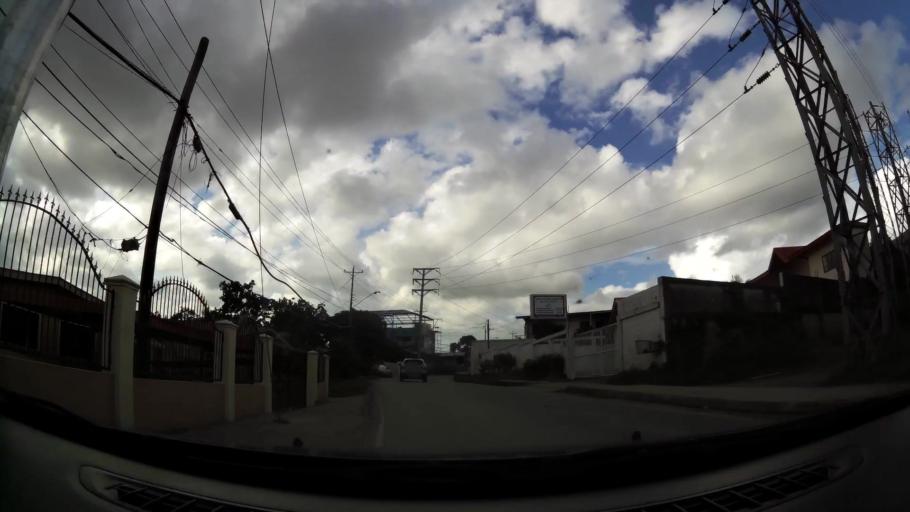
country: TT
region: City of San Fernando
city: Mon Repos
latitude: 10.2741
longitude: -61.4394
